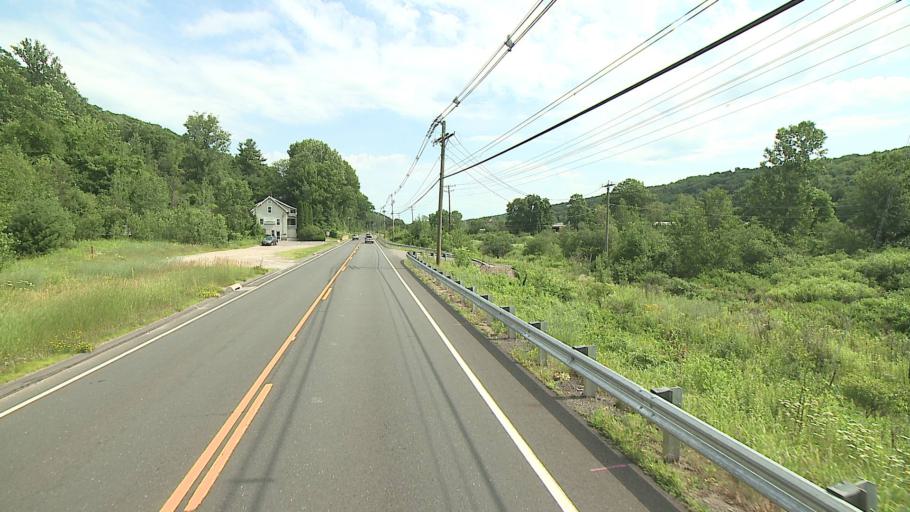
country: US
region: Connecticut
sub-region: Litchfield County
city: Winsted
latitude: 41.8941
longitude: -73.0736
